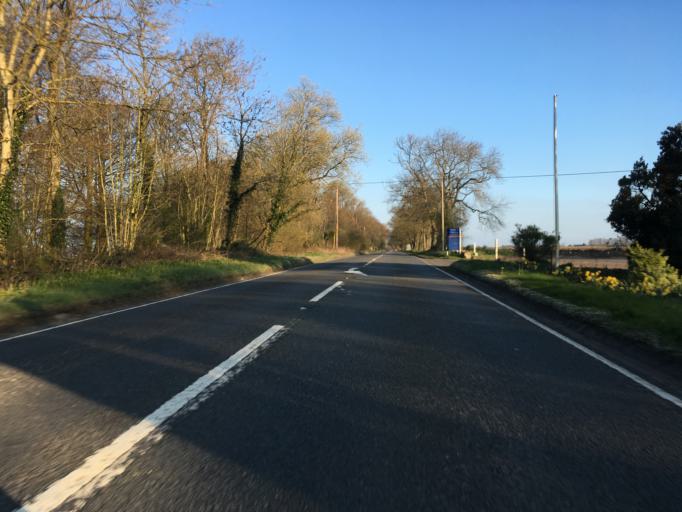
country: GB
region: England
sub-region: Gloucestershire
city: Westfield
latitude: 51.8523
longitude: -1.8922
